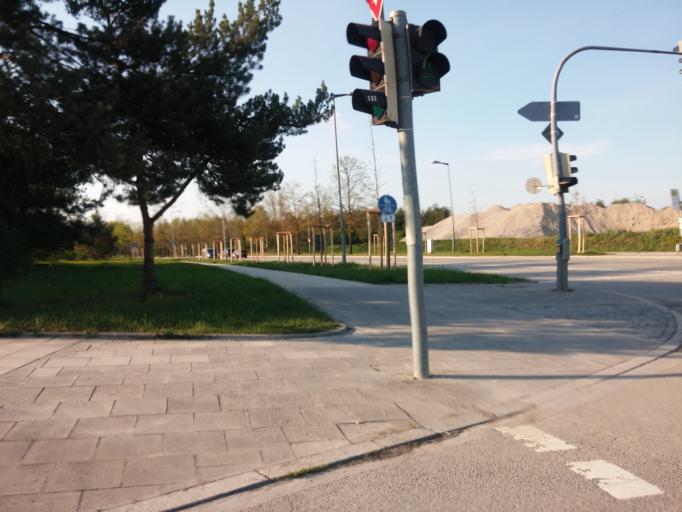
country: DE
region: Bavaria
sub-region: Upper Bavaria
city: Feldkirchen
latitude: 48.1366
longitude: 11.7151
